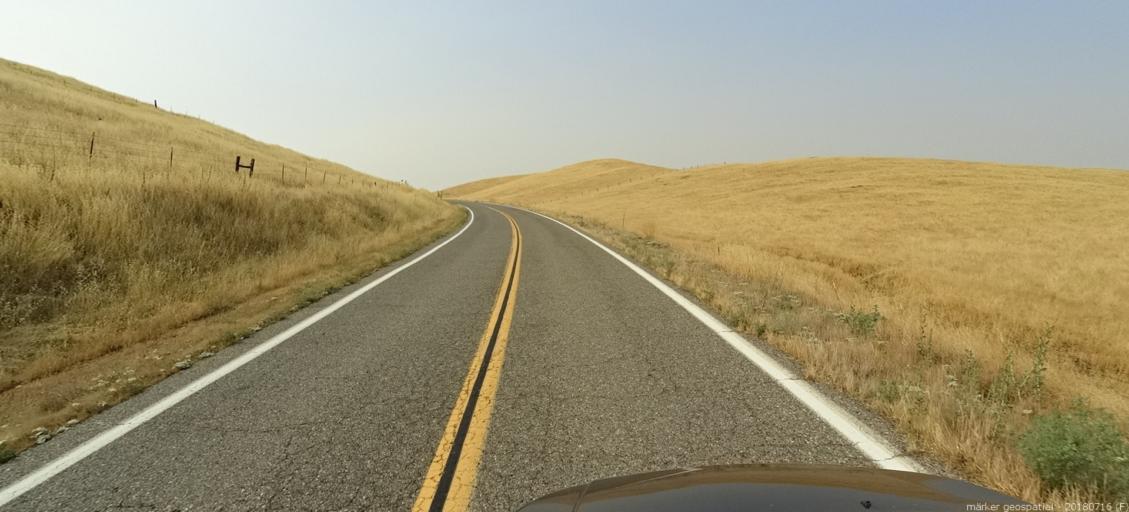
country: US
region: California
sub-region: Madera County
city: Madera Acres
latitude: 37.1865
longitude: -120.0027
